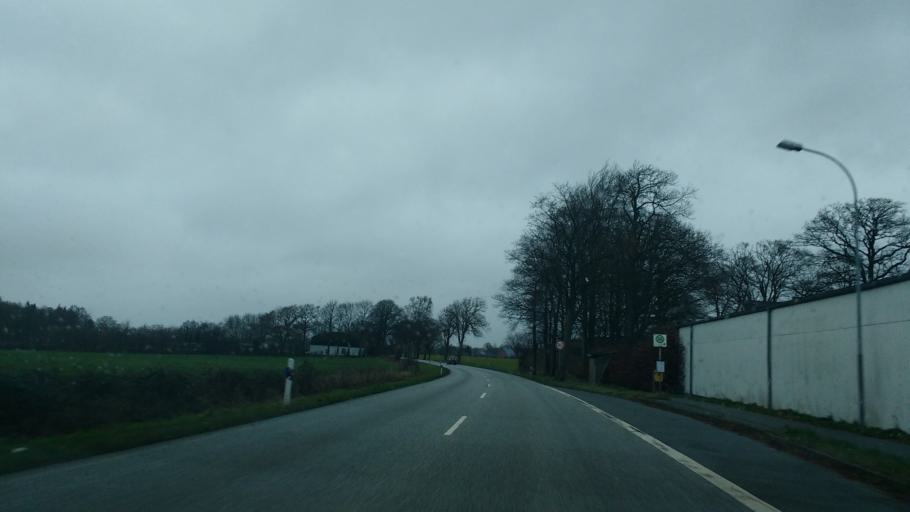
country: DE
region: Schleswig-Holstein
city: Jahrsdorf
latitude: 54.0556
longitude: 9.6324
